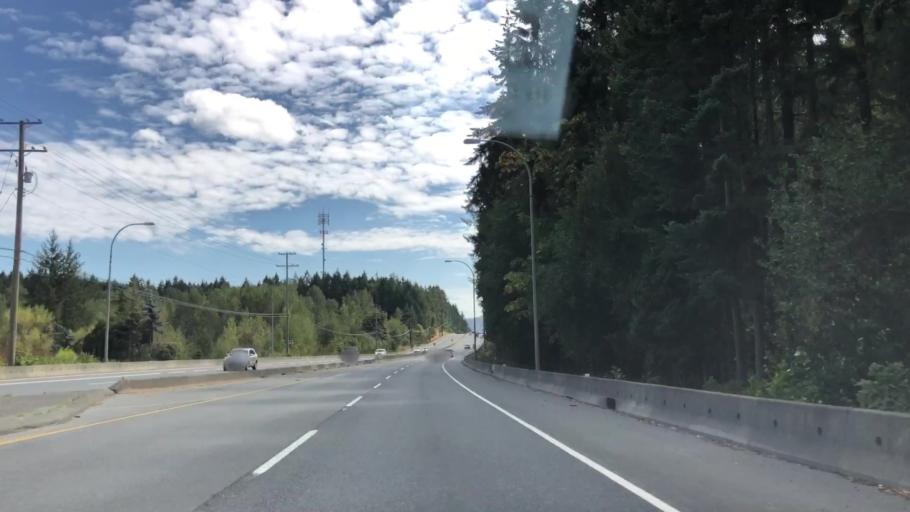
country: CA
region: British Columbia
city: North Cowichan
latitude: 48.9032
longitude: -123.7219
